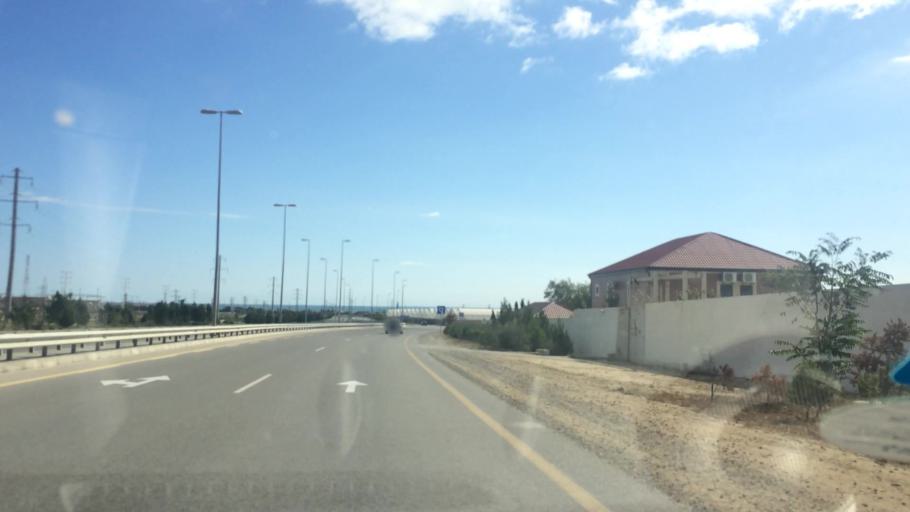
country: AZ
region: Baki
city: Zyrya
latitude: 40.3996
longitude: 50.3178
